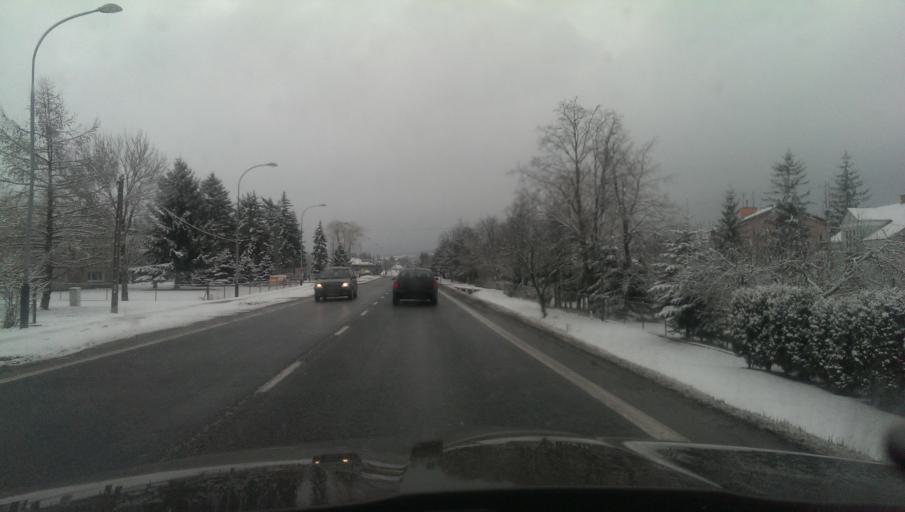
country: PL
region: Subcarpathian Voivodeship
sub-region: Powiat krosnienski
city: Miejsce Piastowe
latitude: 49.6093
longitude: 21.8034
